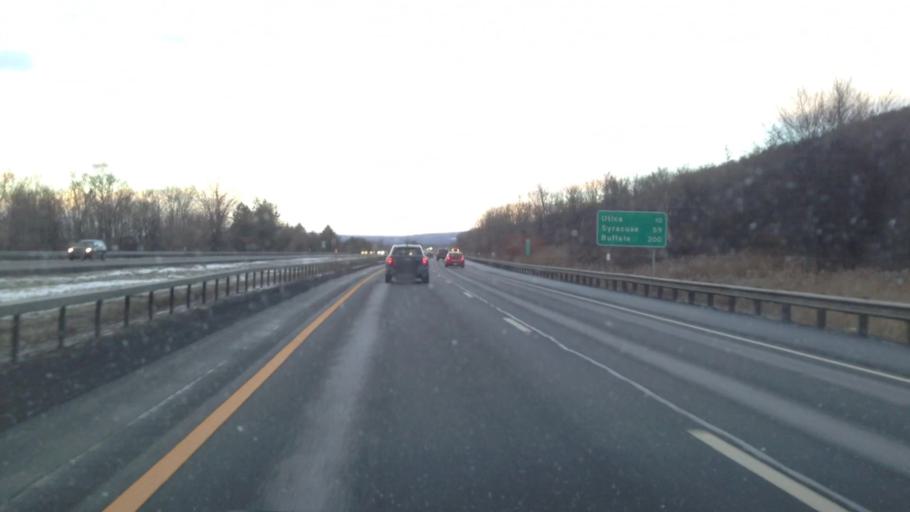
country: US
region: New York
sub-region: Herkimer County
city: Ilion
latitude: 43.0344
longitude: -75.0470
